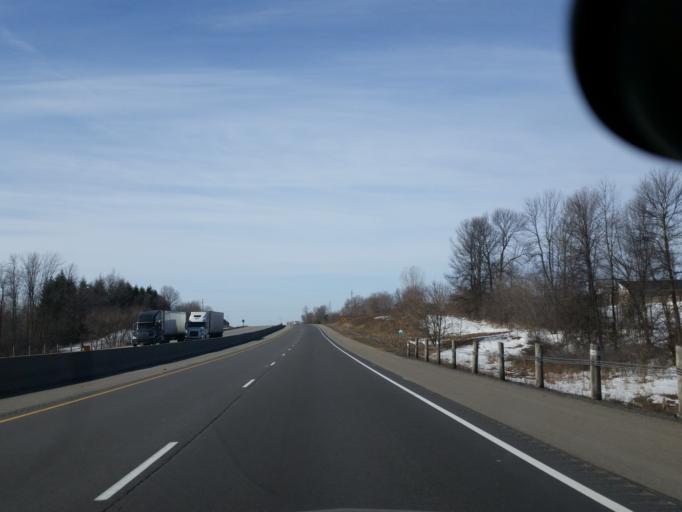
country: CA
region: Ontario
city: Brockville
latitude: 44.6189
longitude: -75.6744
